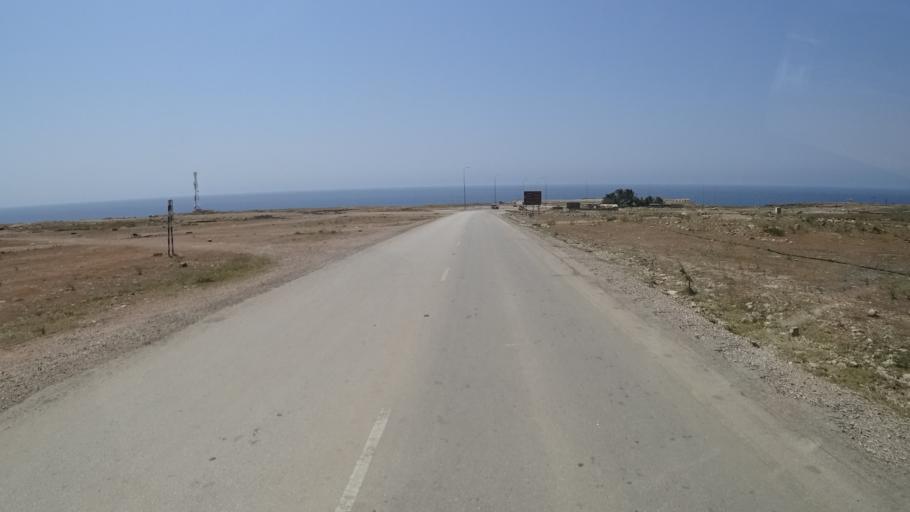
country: OM
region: Zufar
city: Salalah
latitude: 17.0355
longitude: 54.6127
